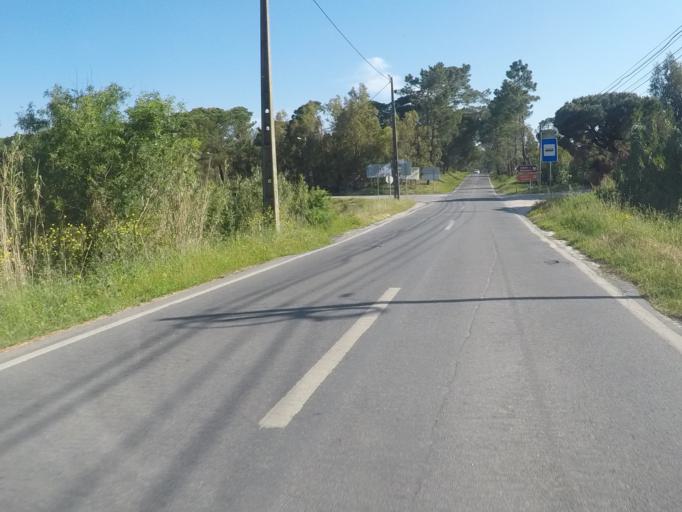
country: PT
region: Setubal
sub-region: Sesimbra
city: Sesimbra
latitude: 38.4846
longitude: -9.1591
